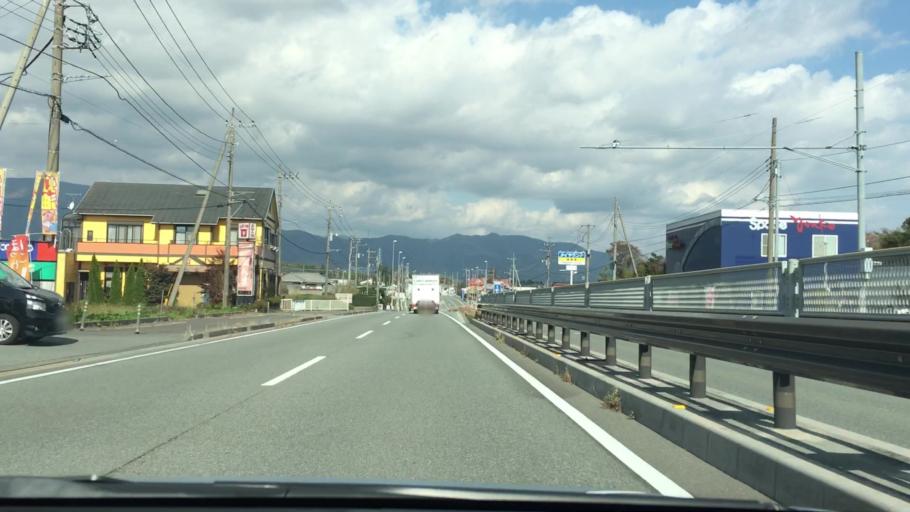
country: JP
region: Shizuoka
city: Gotemba
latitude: 35.3218
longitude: 138.9310
